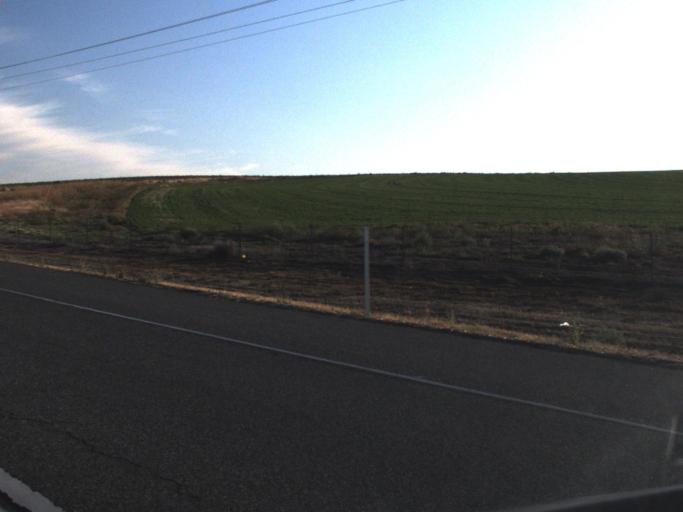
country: US
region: Washington
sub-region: Franklin County
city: Pasco
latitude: 46.3899
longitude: -119.0646
